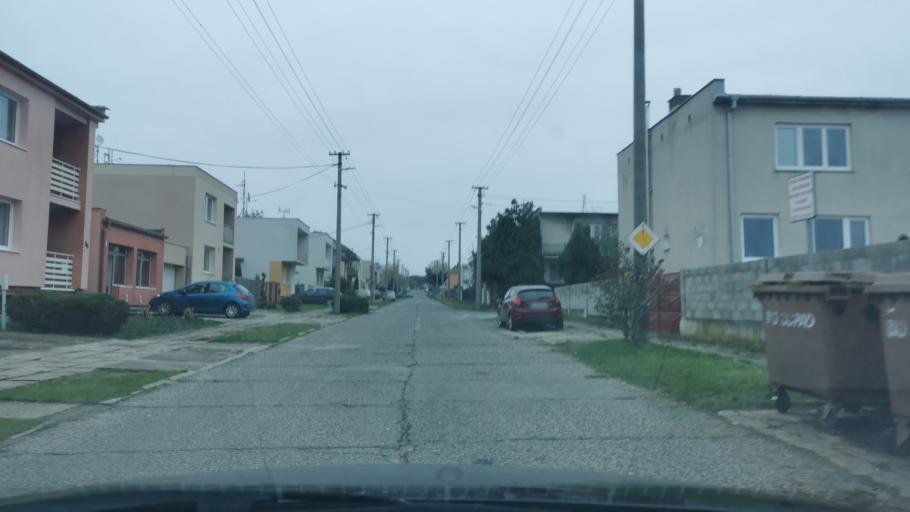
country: SK
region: Trnavsky
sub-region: Okres Skalica
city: Holic
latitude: 48.8181
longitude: 17.1665
